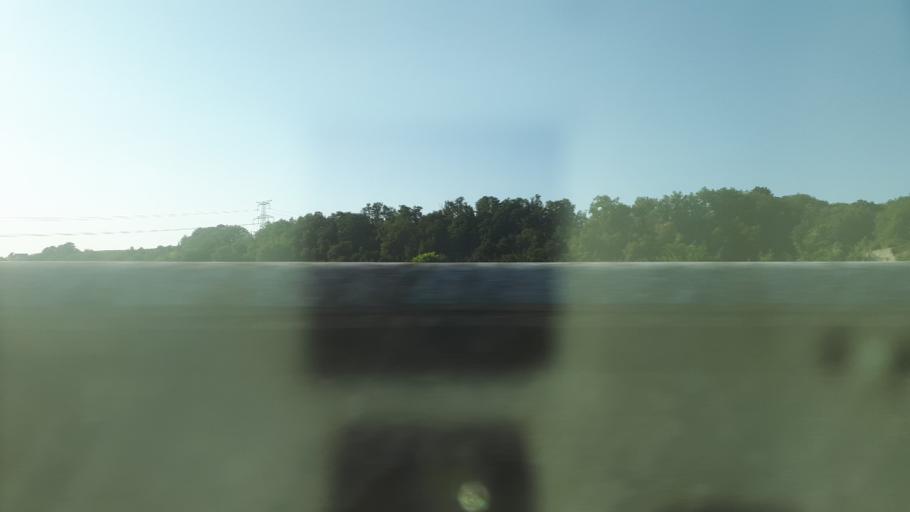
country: FR
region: Centre
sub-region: Departement d'Indre-et-Loire
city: Vouvray
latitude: 47.4116
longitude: 0.8208
